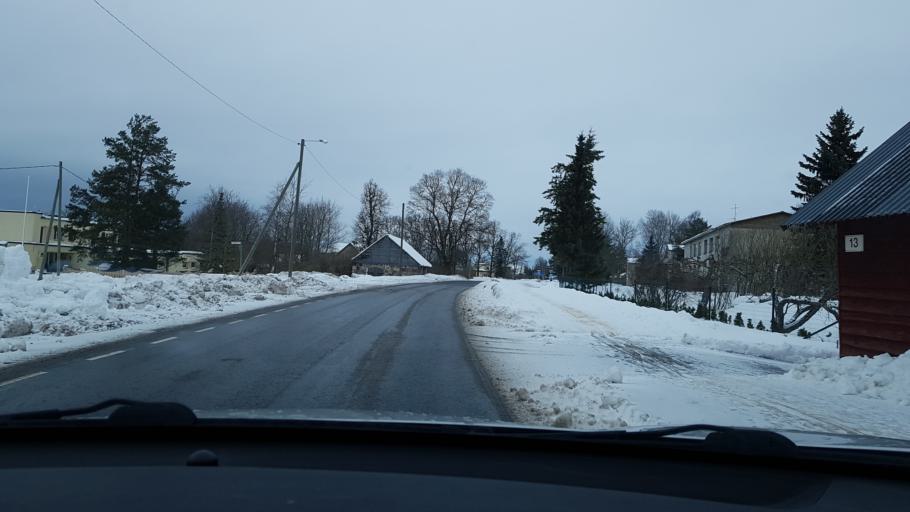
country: EE
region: Jaervamaa
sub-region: Jaerva-Jaani vald
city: Jarva-Jaani
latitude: 59.1468
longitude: 25.7523
